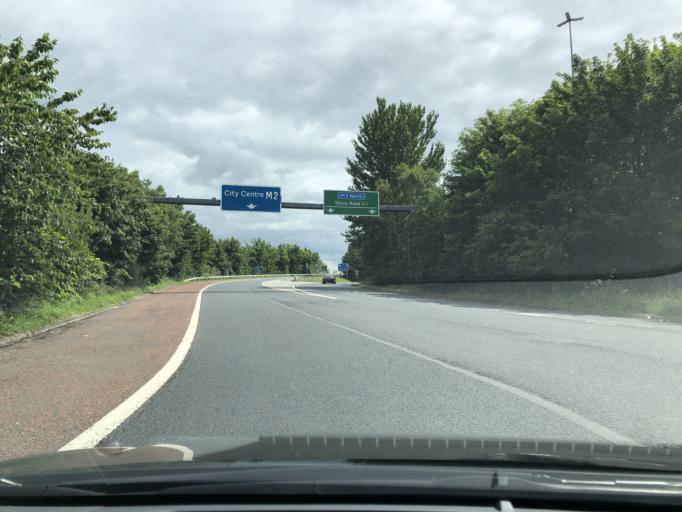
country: GB
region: Northern Ireland
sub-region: Newtownabbey District
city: Newtownabbey
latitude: 54.6490
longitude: -5.9188
